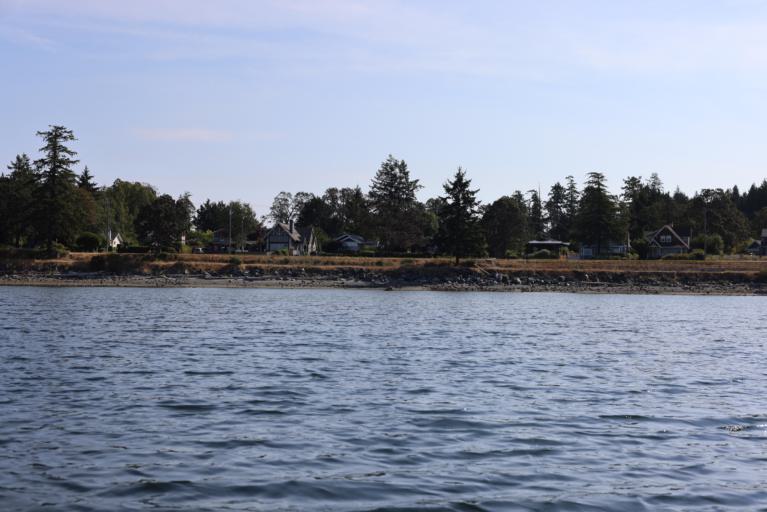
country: CA
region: British Columbia
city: North Saanich
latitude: 48.6571
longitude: -123.4497
